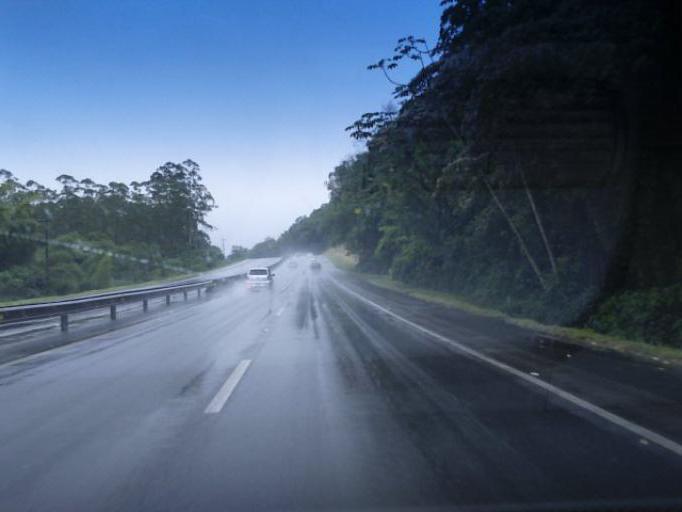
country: BR
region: Santa Catarina
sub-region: Joinville
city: Joinville
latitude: -26.4221
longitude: -48.8300
